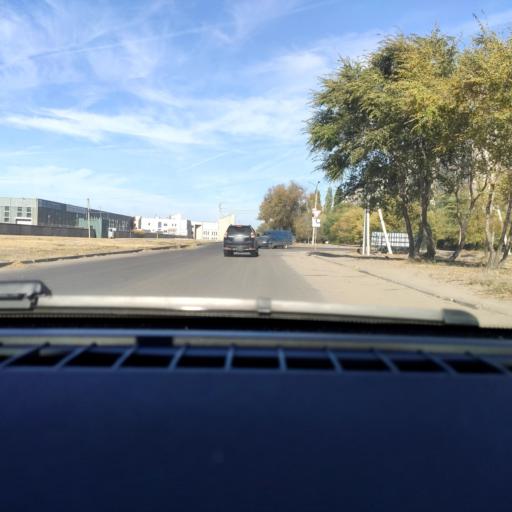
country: RU
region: Voronezj
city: Maslovka
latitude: 51.5941
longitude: 39.2367
